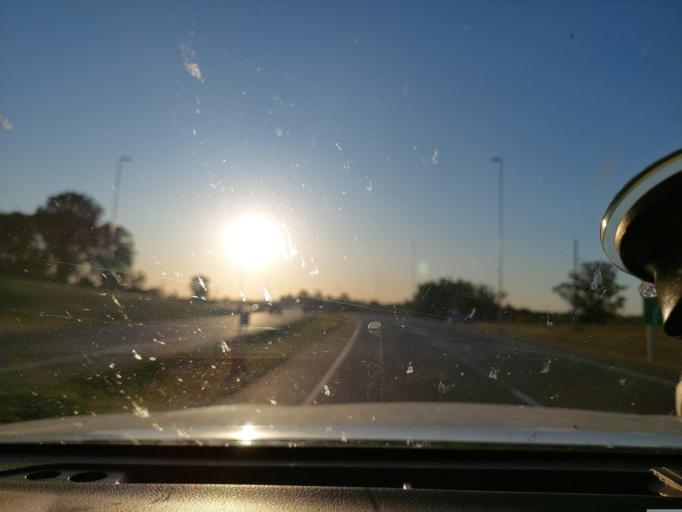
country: UY
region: Canelones
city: Empalme Olmos
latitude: -34.7005
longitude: -55.9169
